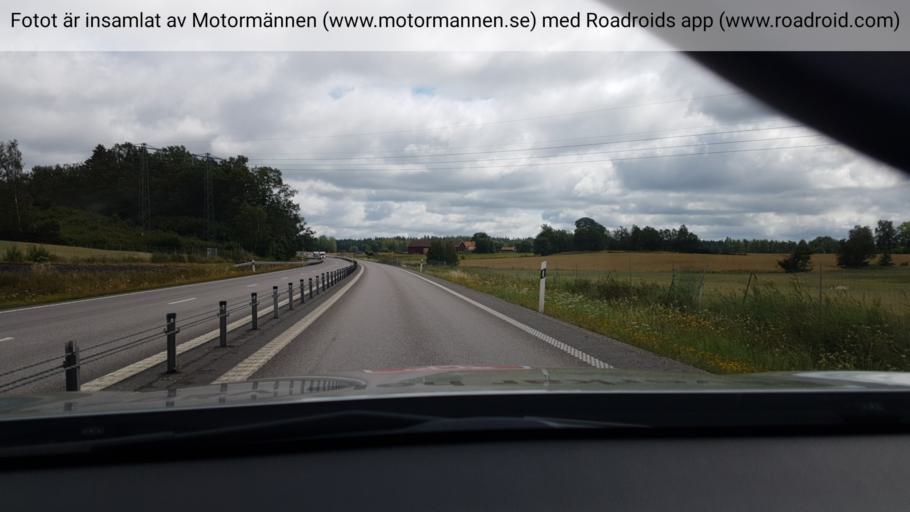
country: SE
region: Vaestra Goetaland
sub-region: Vanersborgs Kommun
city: Vargon
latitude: 58.2817
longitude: 12.4389
